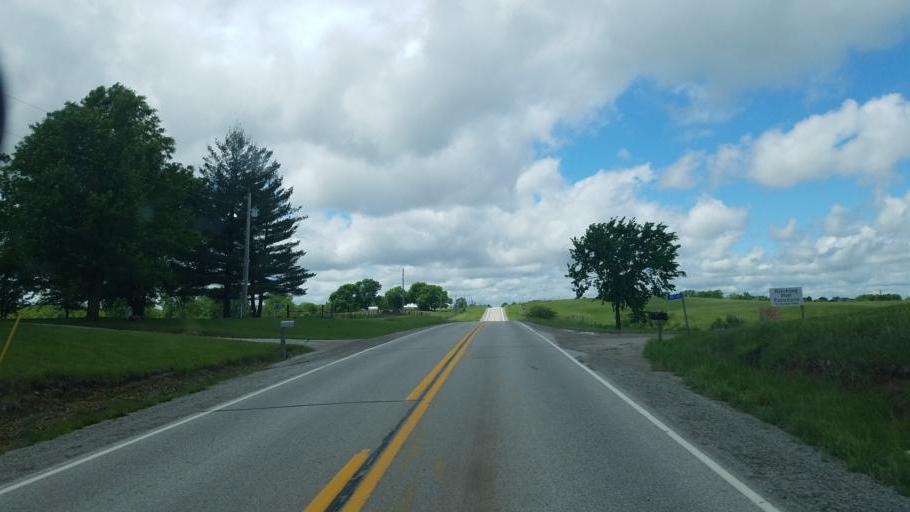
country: US
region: Iowa
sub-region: Decatur County
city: Lamoni
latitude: 40.6238
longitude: -93.8644
